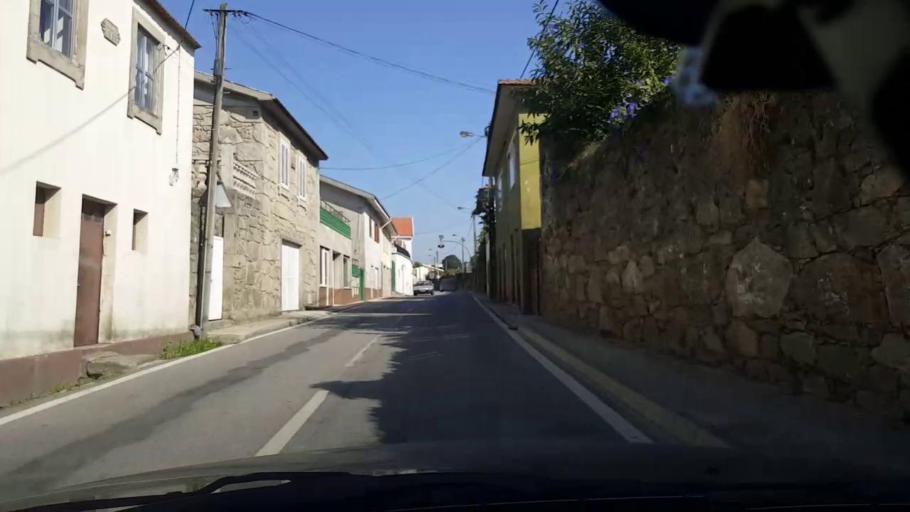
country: PT
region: Porto
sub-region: Maia
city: Gemunde
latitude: 41.3045
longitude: -8.6787
